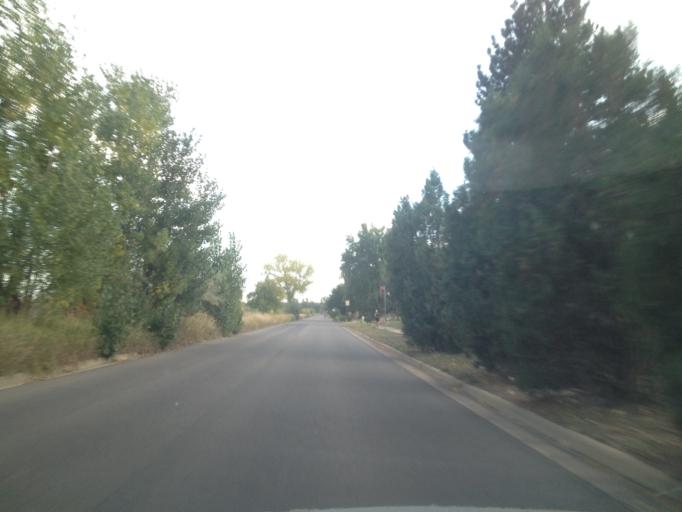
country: US
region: Colorado
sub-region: Boulder County
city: Boulder
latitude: 39.9975
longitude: -105.2244
